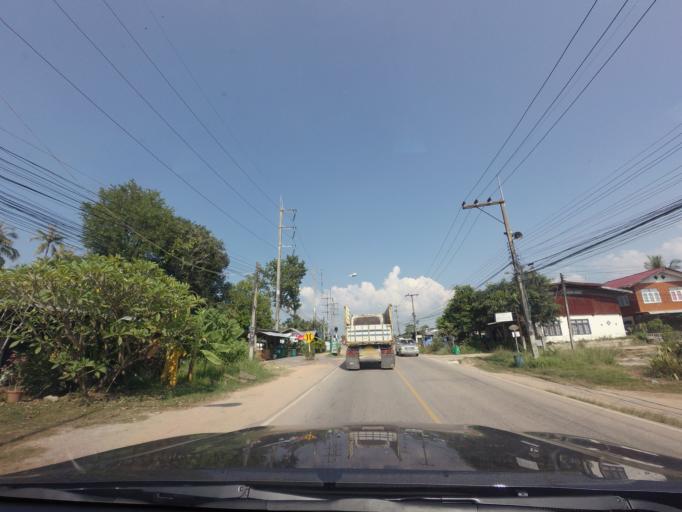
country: TH
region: Phitsanulok
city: Nakhon Thai
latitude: 17.1066
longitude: 100.8443
